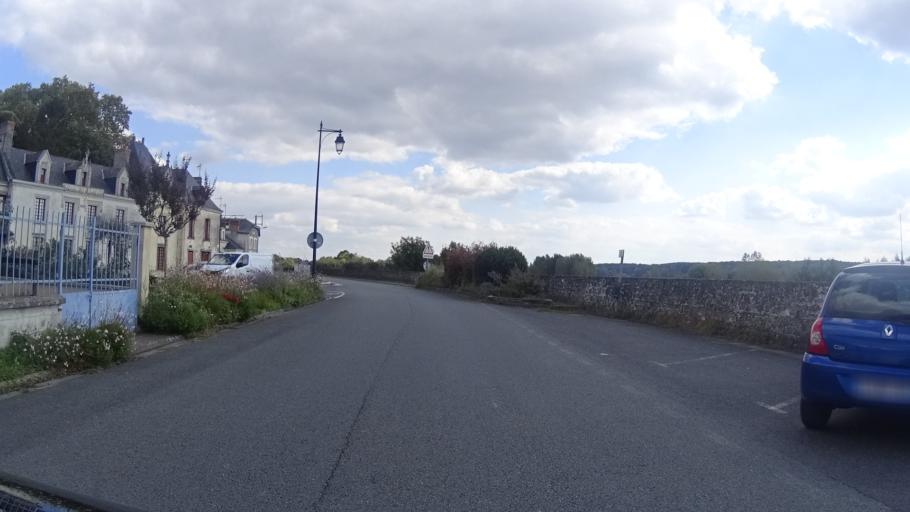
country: FR
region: Pays de la Loire
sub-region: Departement de Maine-et-Loire
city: Les Rosiers-sur-Loire
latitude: 47.3483
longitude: -0.2238
